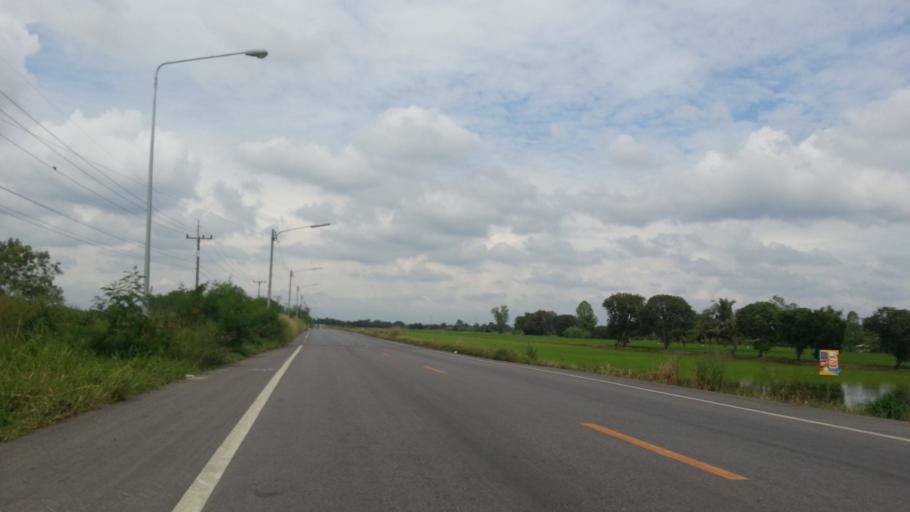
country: TH
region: Pathum Thani
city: Ban Rangsit
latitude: 14.0434
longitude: 100.8444
